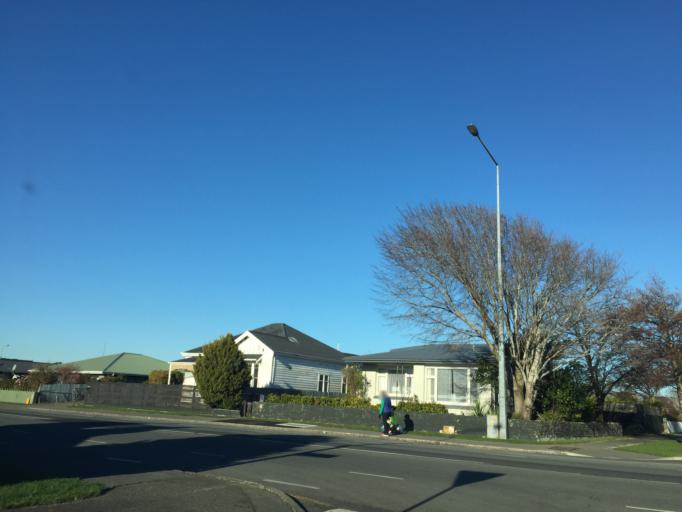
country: NZ
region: Southland
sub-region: Invercargill City
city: Invercargill
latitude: -46.4066
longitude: 168.3726
